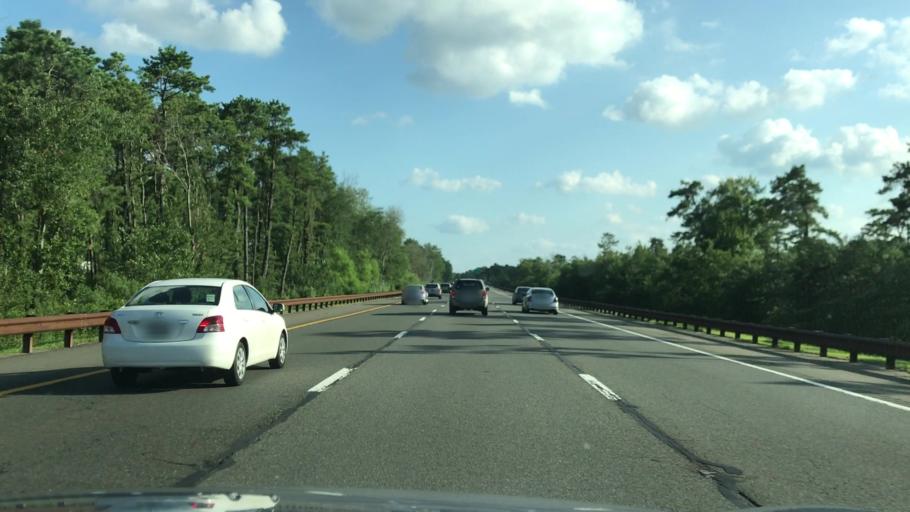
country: US
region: New Jersey
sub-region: Ocean County
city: South Toms River
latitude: 39.9211
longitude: -74.2104
